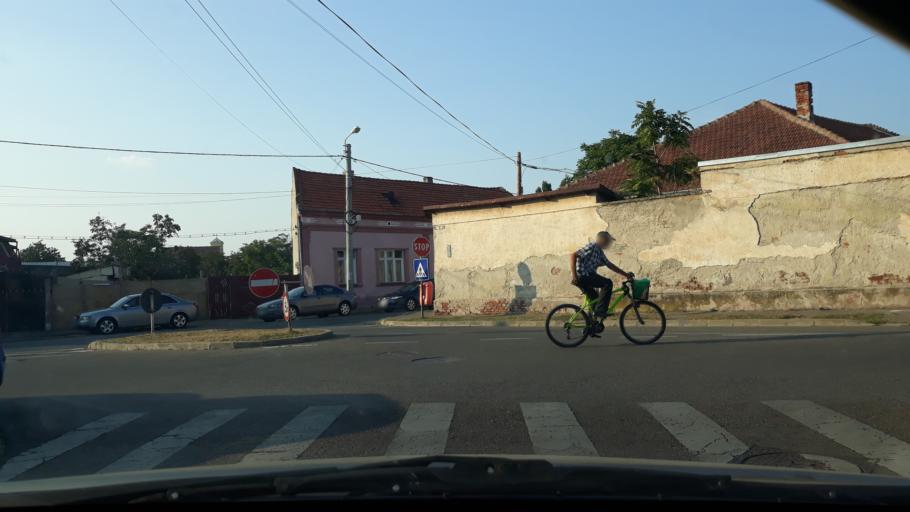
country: RO
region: Bihor
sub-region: Comuna Biharea
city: Oradea
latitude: 47.0482
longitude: 21.9465
